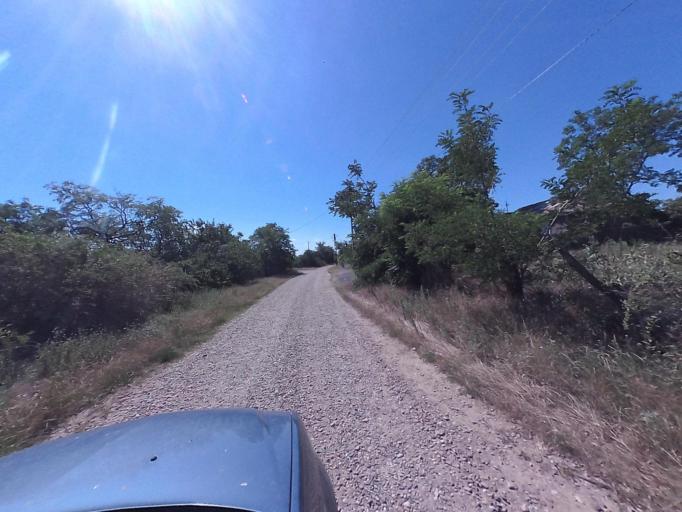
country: RO
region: Vaslui
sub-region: Comuna Costesti
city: Costesti
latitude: 46.4784
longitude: 27.7928
